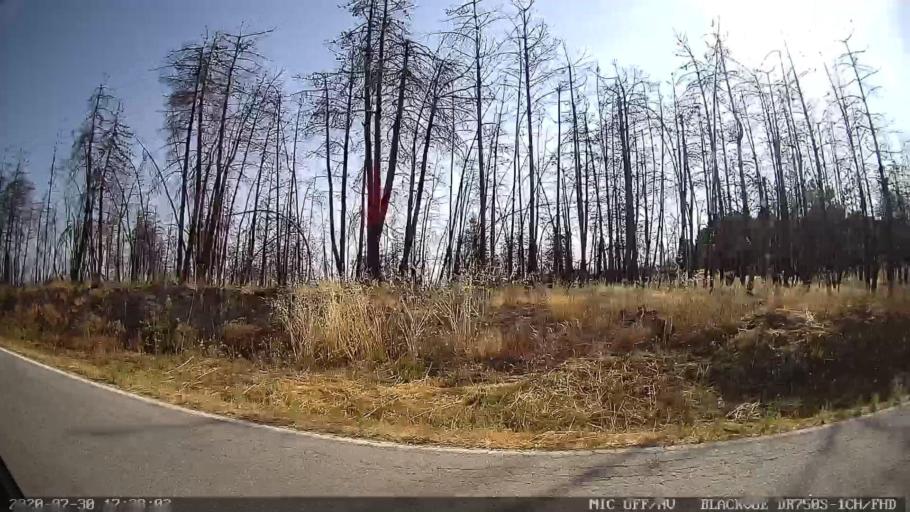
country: PT
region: Vila Real
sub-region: Murca
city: Murca
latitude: 41.3696
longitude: -7.4983
